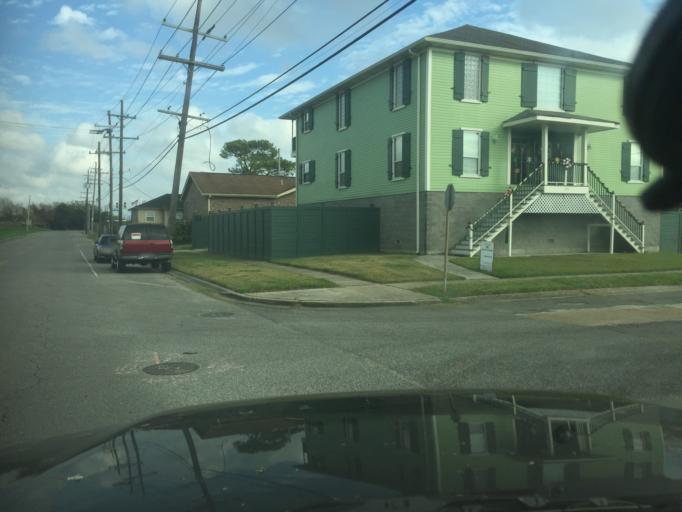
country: US
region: Louisiana
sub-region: Orleans Parish
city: New Orleans
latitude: 29.9919
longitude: -90.0797
